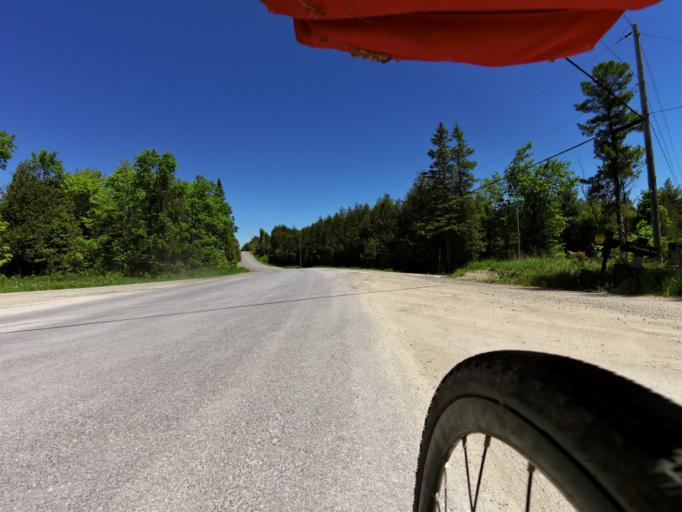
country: CA
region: Ontario
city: Carleton Place
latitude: 45.1613
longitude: -76.4306
